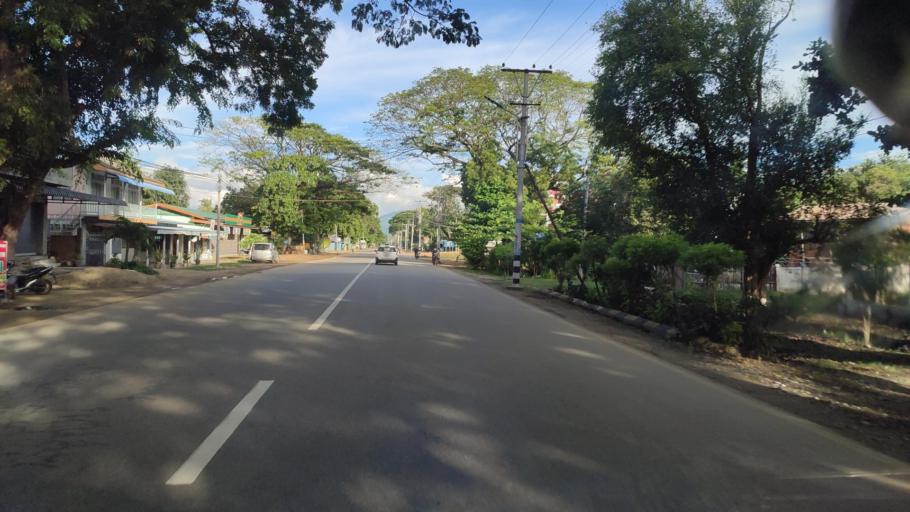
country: MM
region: Mandalay
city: Yamethin
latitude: 20.1256
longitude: 96.2070
